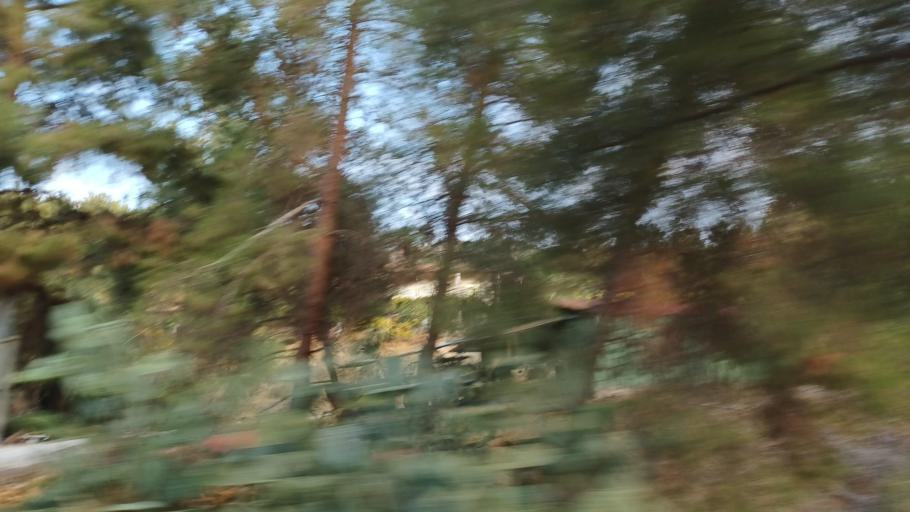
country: CY
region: Lefkosia
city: Kakopetria
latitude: 35.0215
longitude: 32.8986
